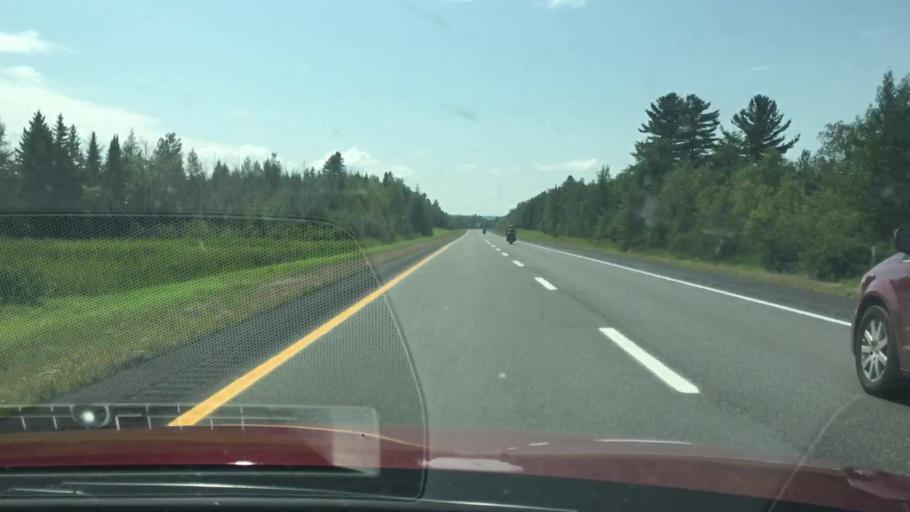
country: US
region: Maine
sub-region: Penobscot County
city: Patten
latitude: 45.9819
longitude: -68.2889
